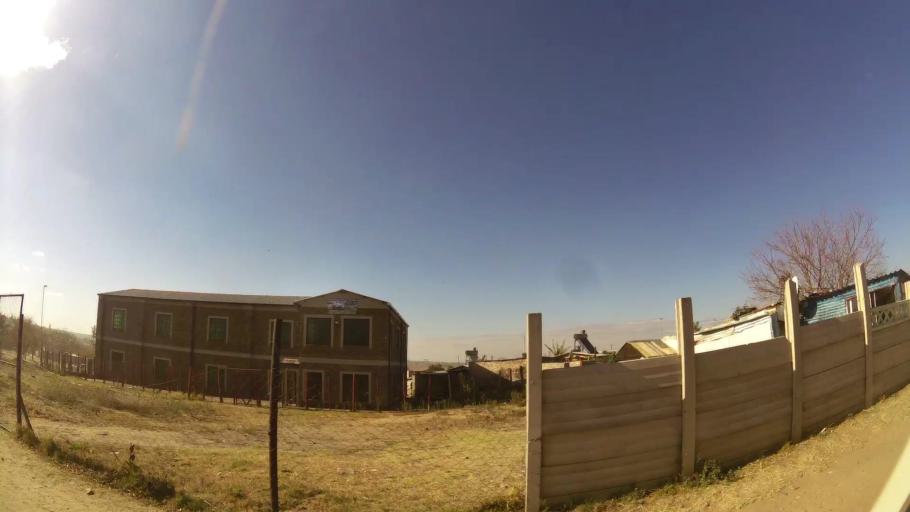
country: ZA
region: Gauteng
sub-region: City of Johannesburg Metropolitan Municipality
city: Diepsloot
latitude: -25.9124
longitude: 28.0892
